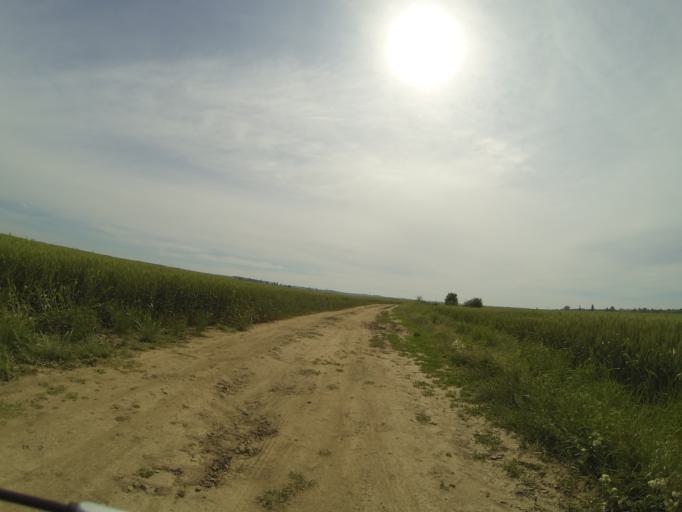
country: RO
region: Dolj
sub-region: Comuna Malu Mare
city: Preajba
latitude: 44.2715
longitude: 23.8512
